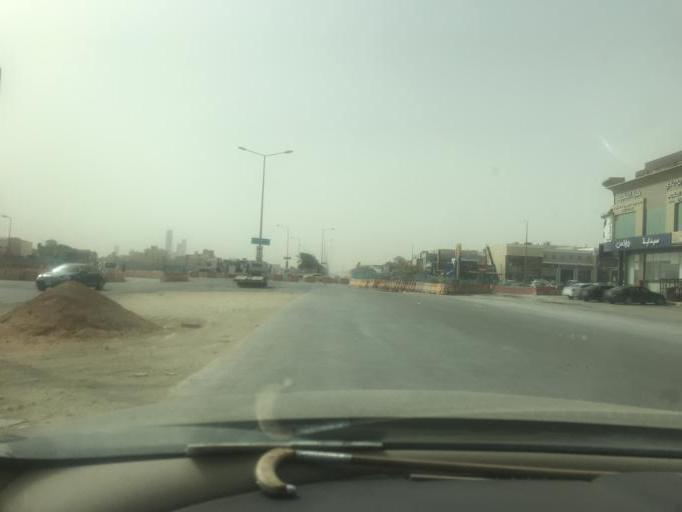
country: SA
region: Ar Riyad
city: Riyadh
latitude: 24.8034
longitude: 46.6039
